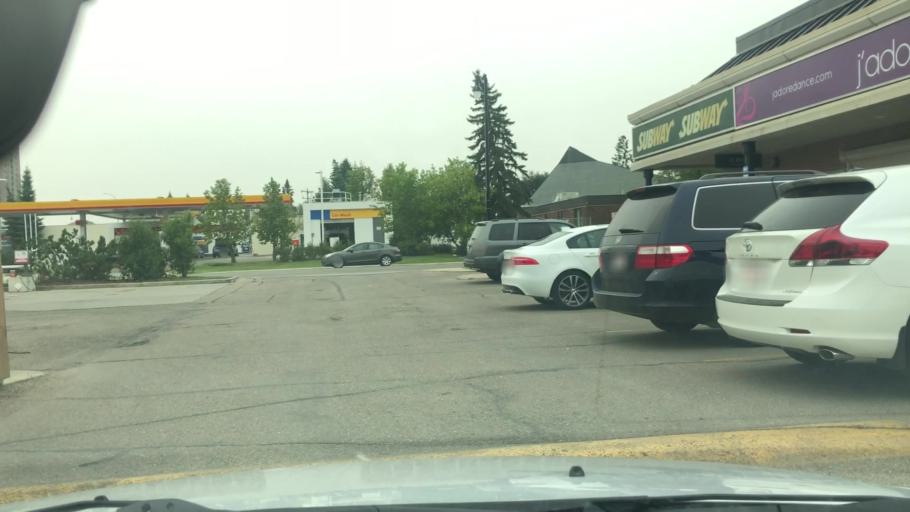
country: CA
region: Alberta
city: Edmonton
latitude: 53.4945
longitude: -113.5176
